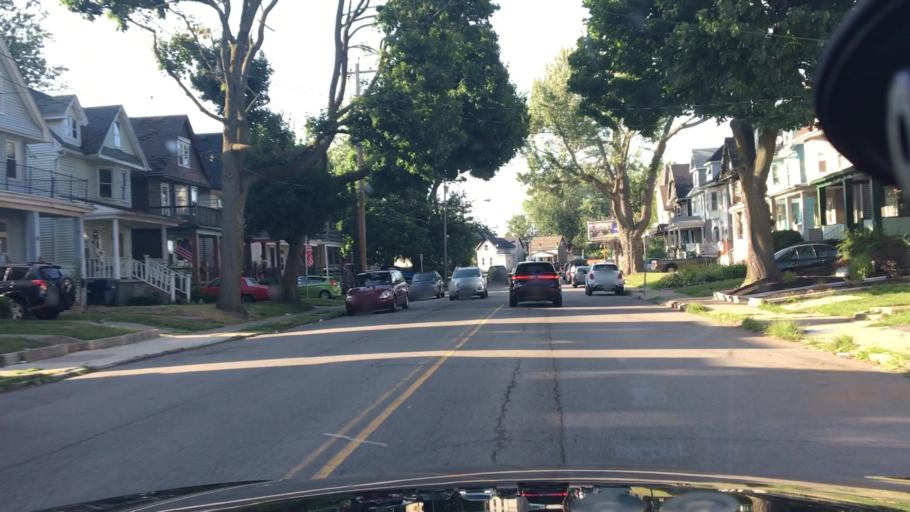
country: US
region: New York
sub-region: Erie County
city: Lackawanna
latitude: 42.8566
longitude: -78.8322
